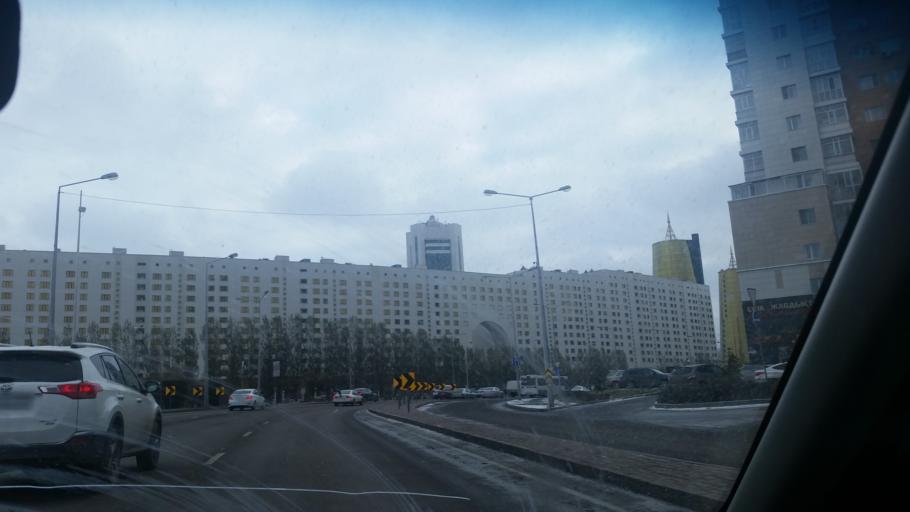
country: KZ
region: Astana Qalasy
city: Astana
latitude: 51.1316
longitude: 71.4394
